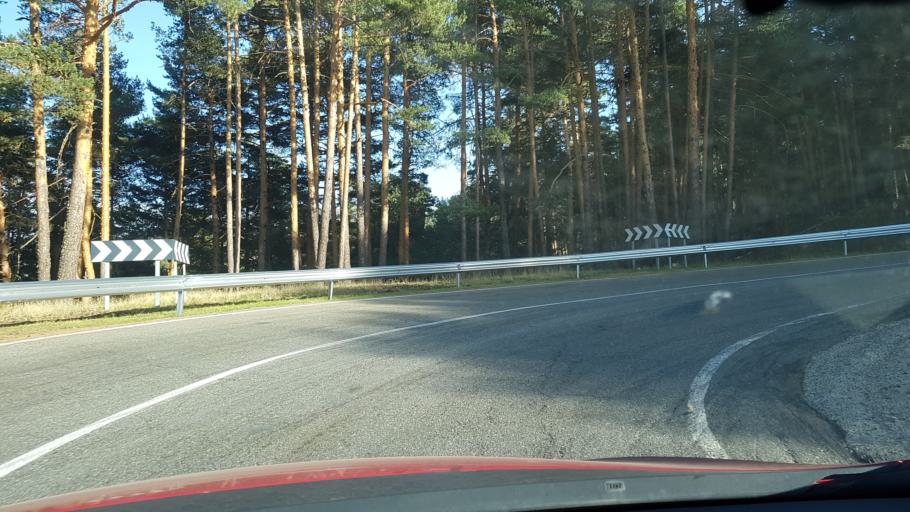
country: ES
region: Madrid
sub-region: Provincia de Madrid
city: Cercedilla
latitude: 40.8145
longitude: -4.0159
